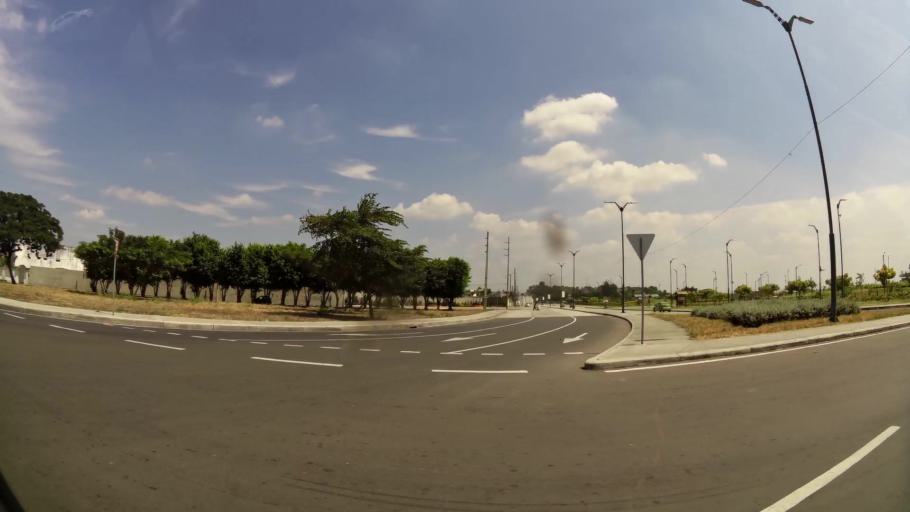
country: EC
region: Guayas
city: Eloy Alfaro
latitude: -2.1067
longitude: -79.8991
